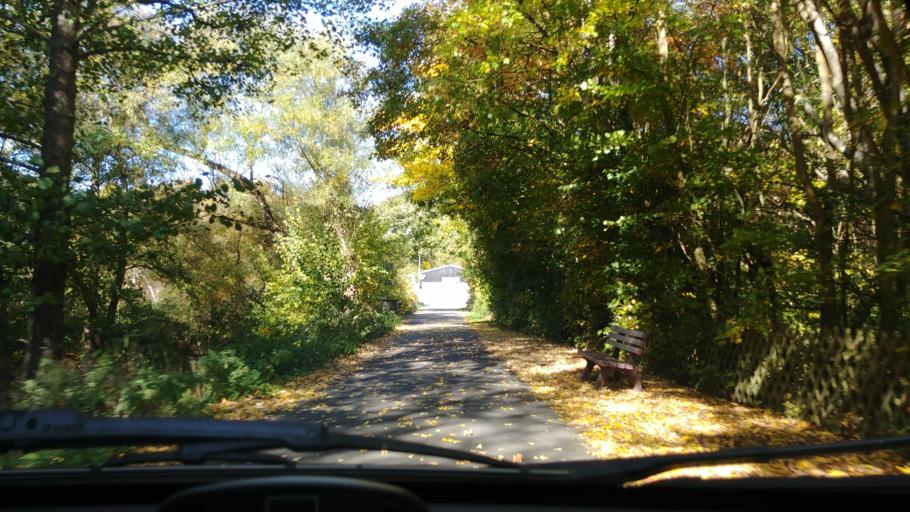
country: DE
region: Rheinland-Pfalz
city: Schiesheim
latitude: 50.2887
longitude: 8.0646
